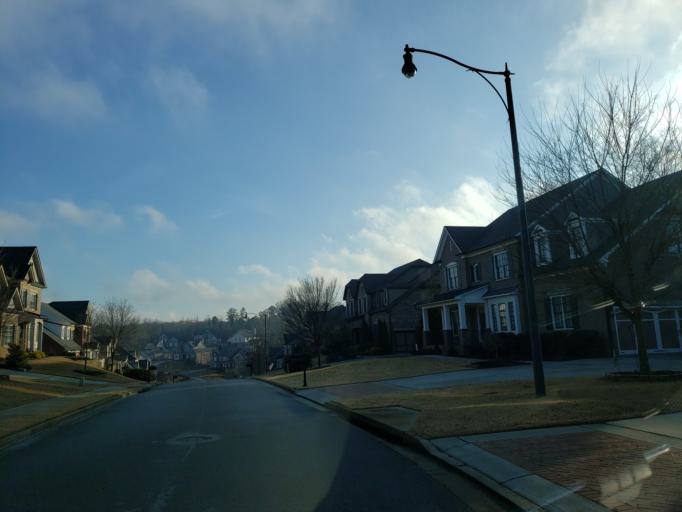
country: US
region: Georgia
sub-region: Cobb County
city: Kennesaw
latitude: 33.9871
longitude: -84.5944
